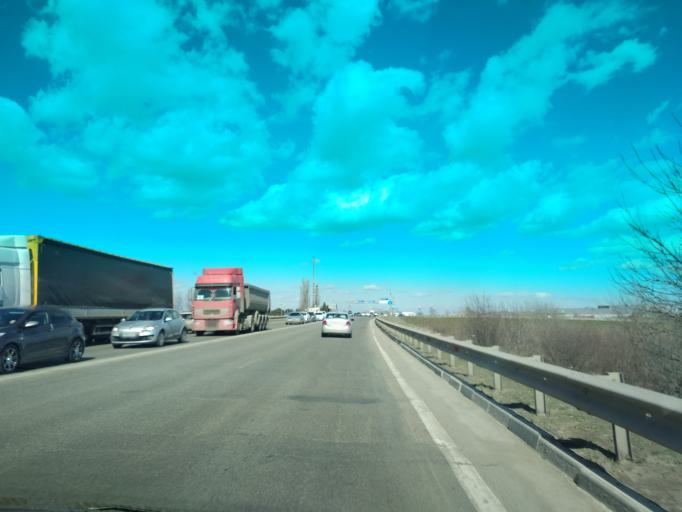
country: RU
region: Krasnodarskiy
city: Pashkovskiy
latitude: 45.0036
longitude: 39.1153
